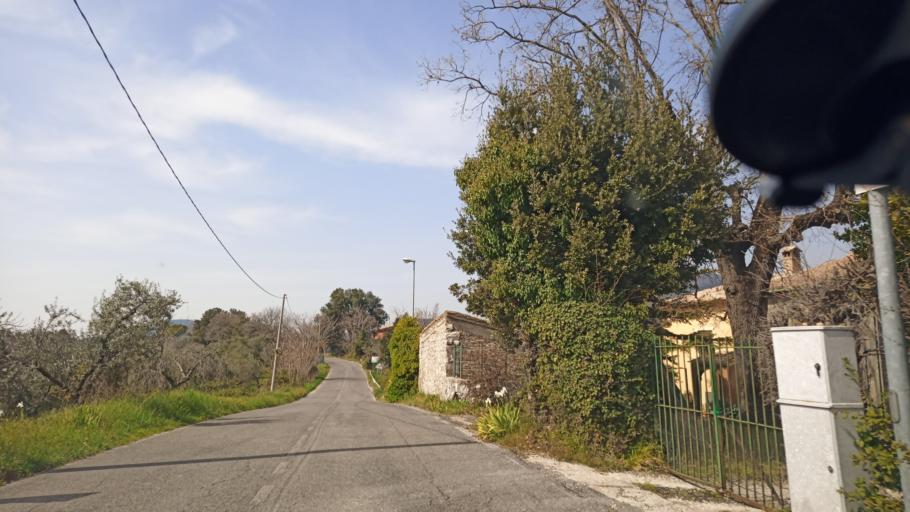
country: IT
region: Latium
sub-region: Provincia di Rieti
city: Montasola
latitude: 42.3645
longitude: 12.6704
